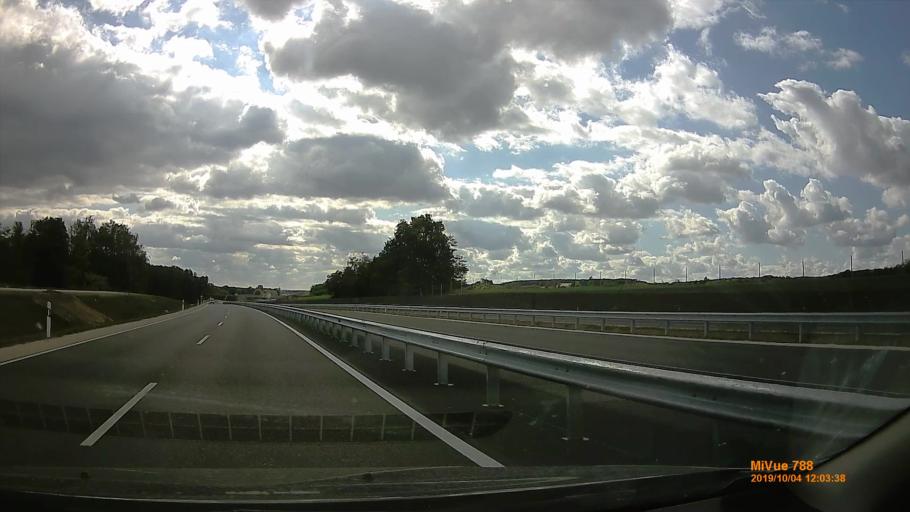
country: HU
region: Somogy
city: Karad
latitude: 46.5849
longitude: 17.8038
